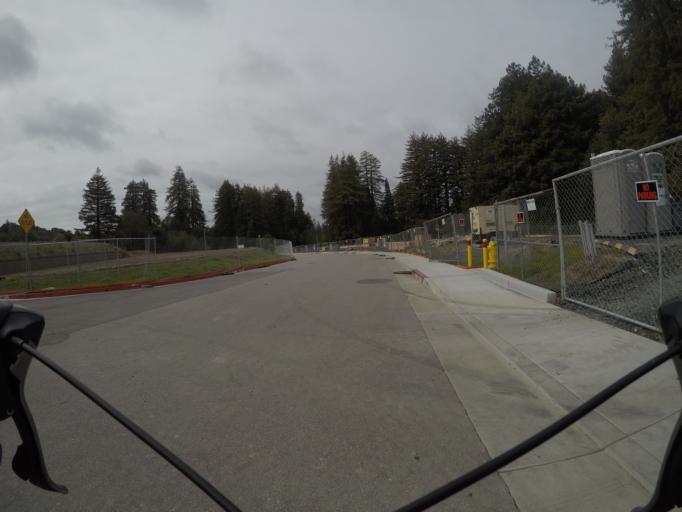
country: US
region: California
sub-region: Santa Cruz County
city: Scotts Valley
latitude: 37.0665
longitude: -121.9950
